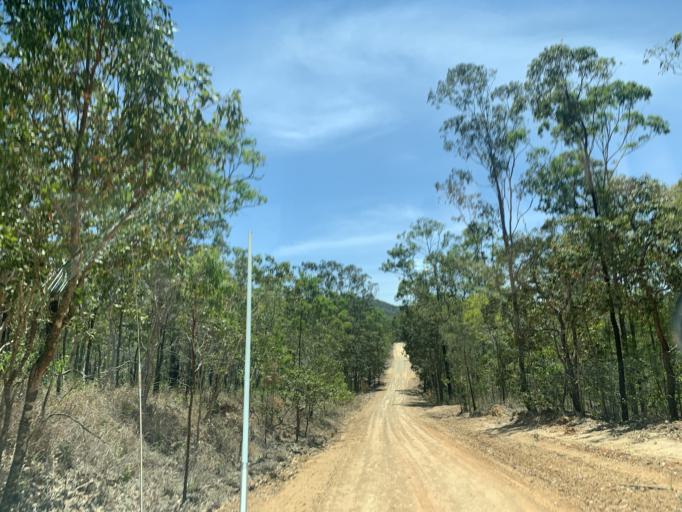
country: AU
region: Queensland
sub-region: Cairns
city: Redlynch
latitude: -16.9207
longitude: 145.5999
